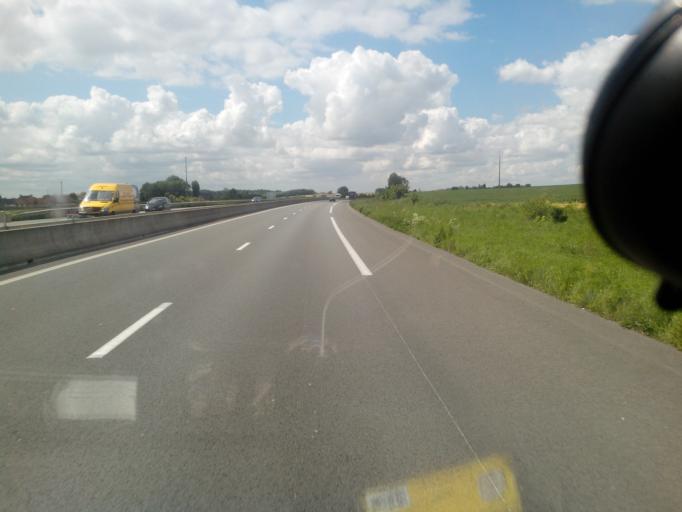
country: FR
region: Nord-Pas-de-Calais
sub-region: Departement du Nord
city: Godewaersvelde
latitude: 50.7554
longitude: 2.6512
